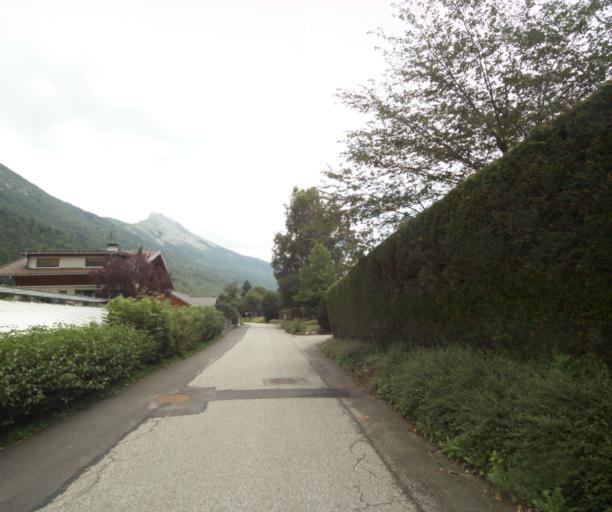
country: FR
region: Rhone-Alpes
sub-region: Departement de la Haute-Savoie
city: Thones
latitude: 45.8866
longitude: 6.3310
